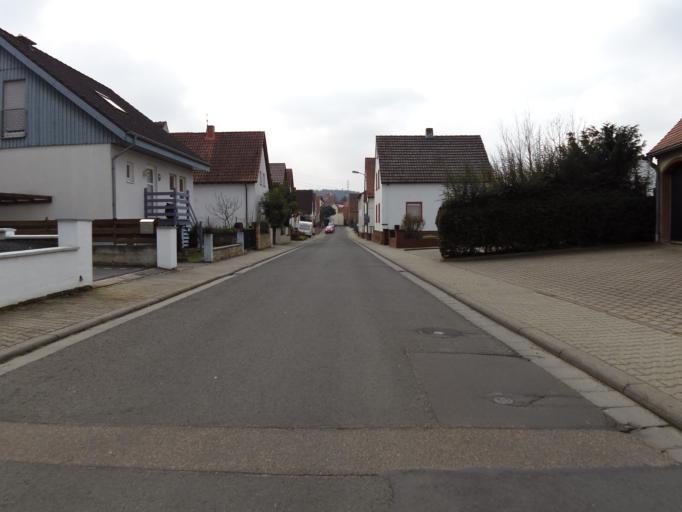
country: DE
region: Rheinland-Pfalz
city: Grunstadt
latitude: 49.5803
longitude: 8.1637
